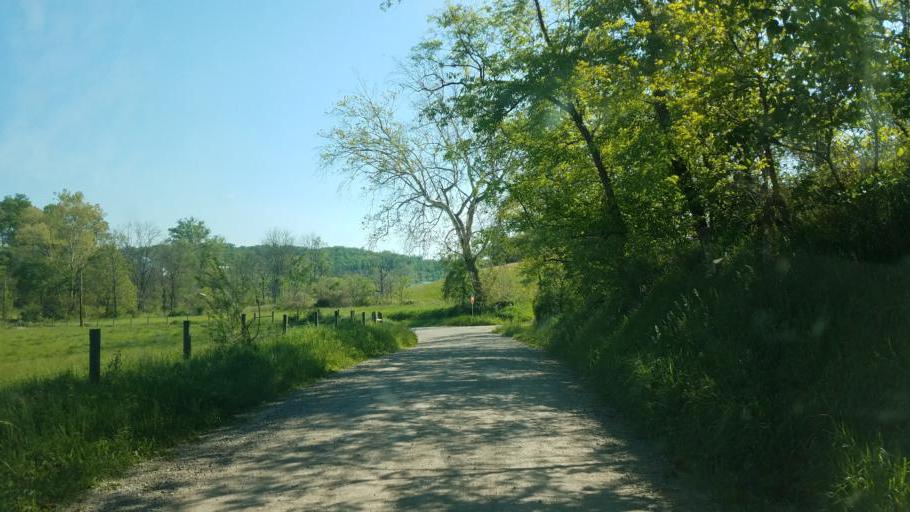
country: US
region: Ohio
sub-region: Belmont County
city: Barnesville
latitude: 40.0576
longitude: -81.3415
